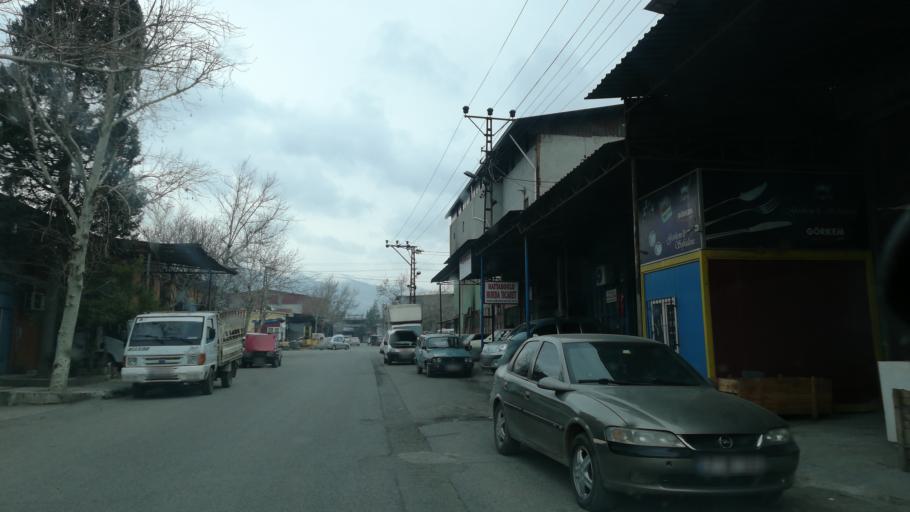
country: TR
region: Kahramanmaras
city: Kahramanmaras
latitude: 37.5585
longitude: 36.9594
